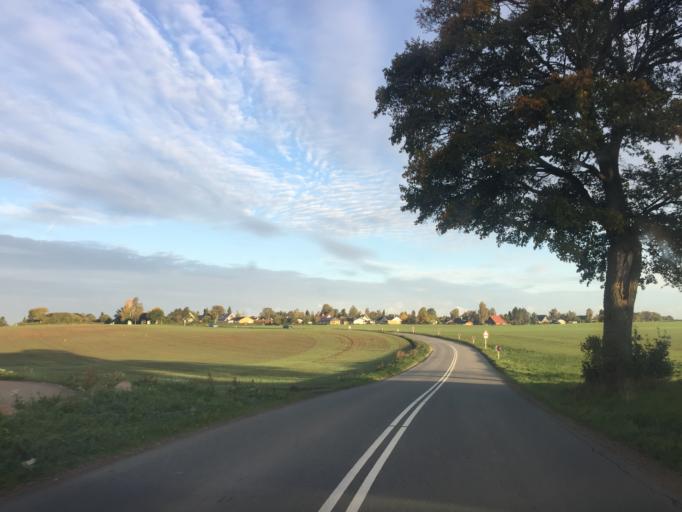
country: DK
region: Capital Region
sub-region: Egedal Kommune
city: Ganlose
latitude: 55.7847
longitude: 12.2774
